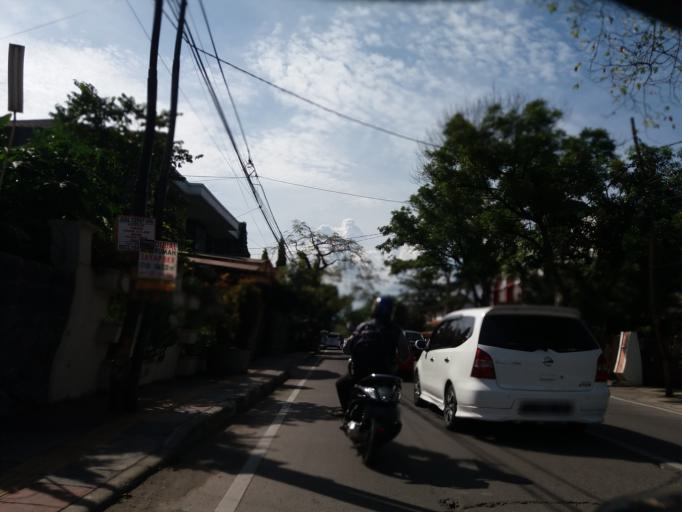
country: ID
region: West Java
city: Bandung
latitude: -6.9423
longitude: 107.6128
